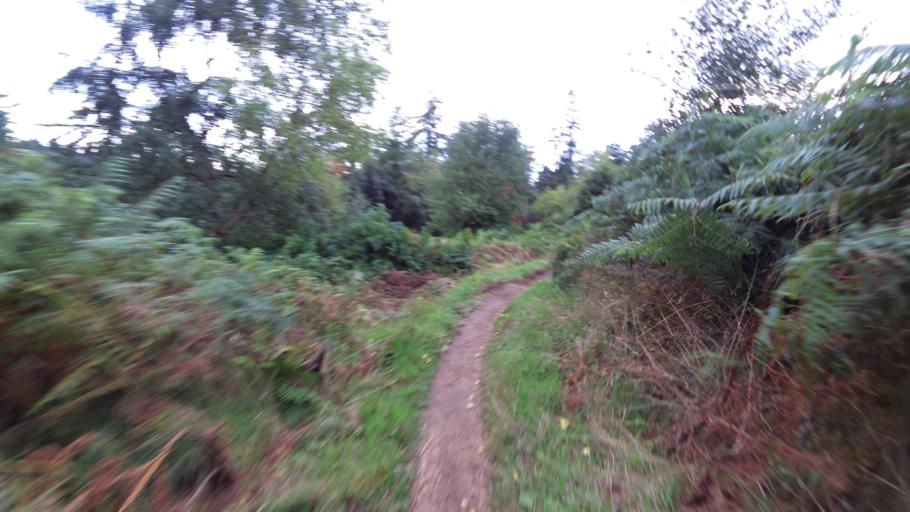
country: GB
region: England
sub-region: North Yorkshire
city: Thornton Dale
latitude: 54.2839
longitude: -0.6810
